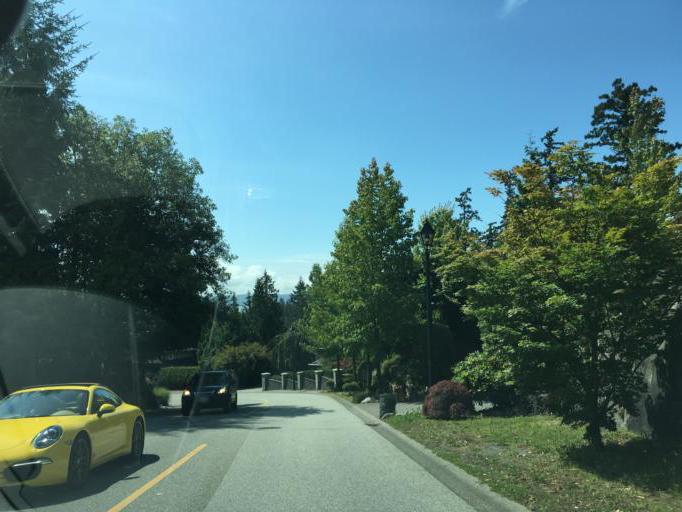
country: CA
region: British Columbia
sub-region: Greater Vancouver Regional District
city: Bowen Island
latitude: 49.3435
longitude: -123.2580
